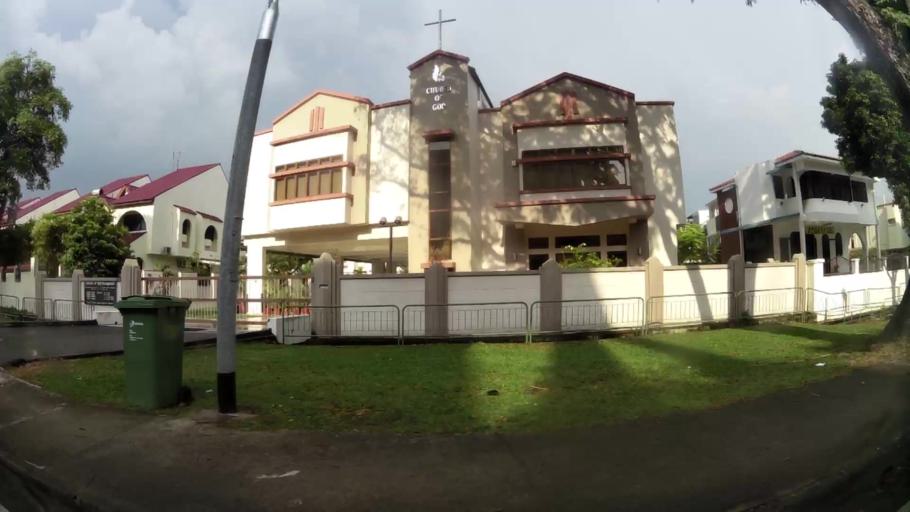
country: SG
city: Singapore
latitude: 1.3262
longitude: 103.9516
